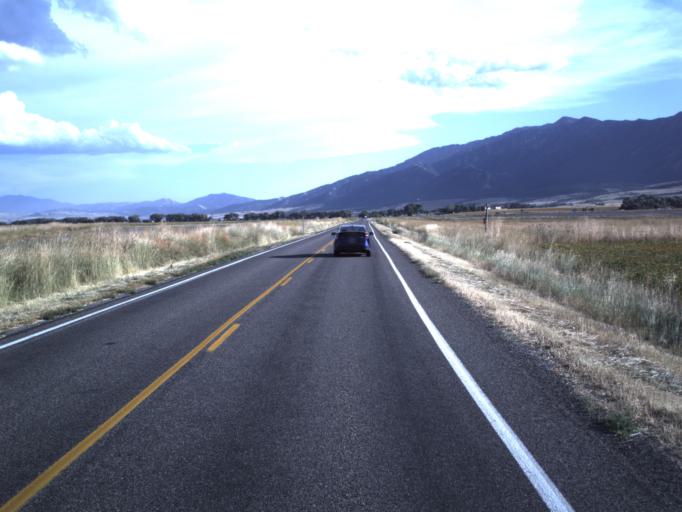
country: US
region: Utah
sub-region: Cache County
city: Mendon
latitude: 41.7615
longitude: -111.9794
